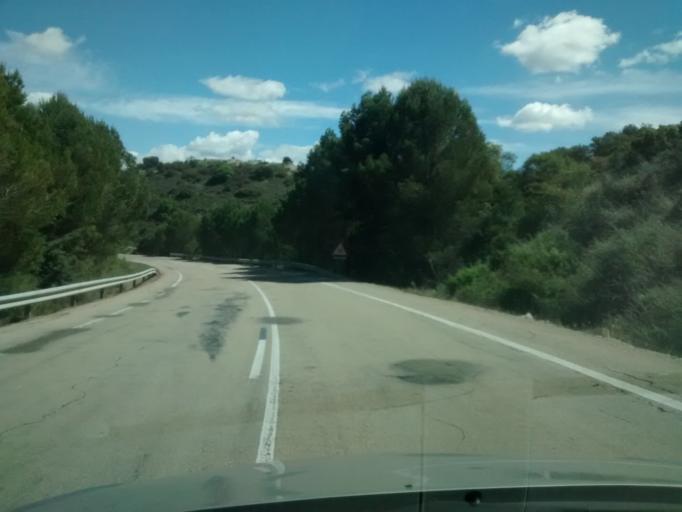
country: ES
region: Aragon
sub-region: Provincia de Huesca
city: Alcubierre
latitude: 41.8204
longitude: -0.5119
